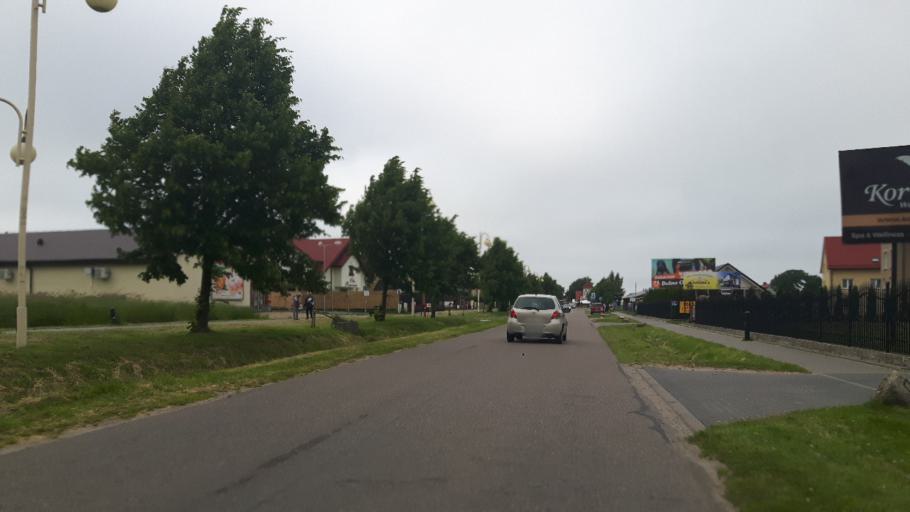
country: PL
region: Pomeranian Voivodeship
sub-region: Powiat slupski
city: Smoldzino
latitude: 54.6621
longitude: 17.0522
